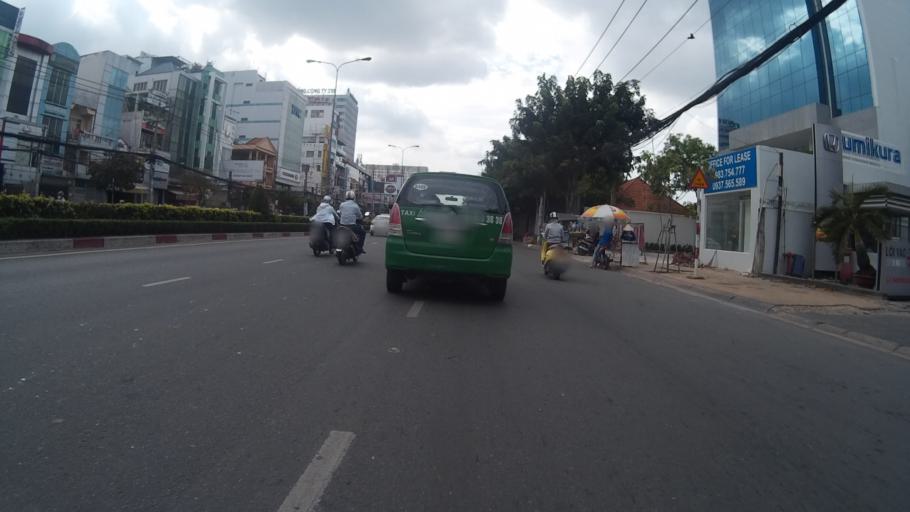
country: VN
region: Ho Chi Minh City
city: Quan Phu Nhuan
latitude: 10.8013
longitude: 106.6557
